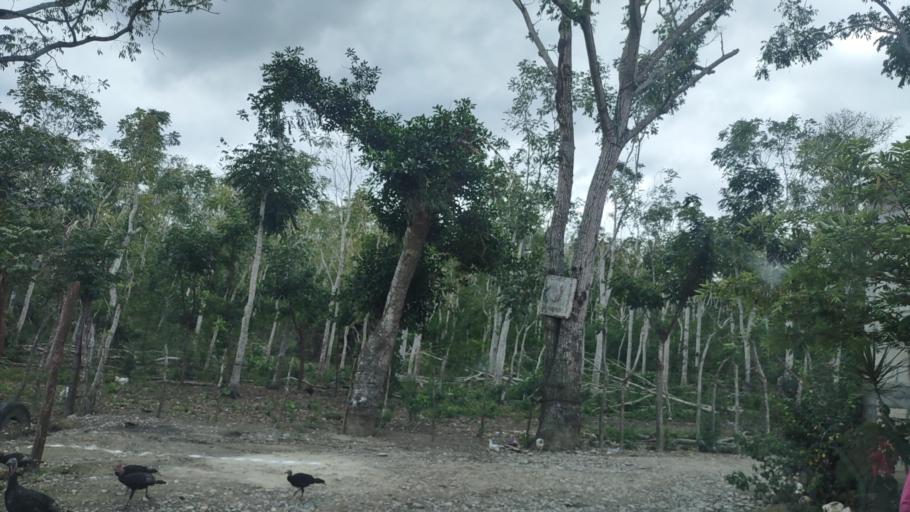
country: MX
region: Veracruz
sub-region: Papantla
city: Polutla
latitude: 20.4641
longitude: -97.2565
